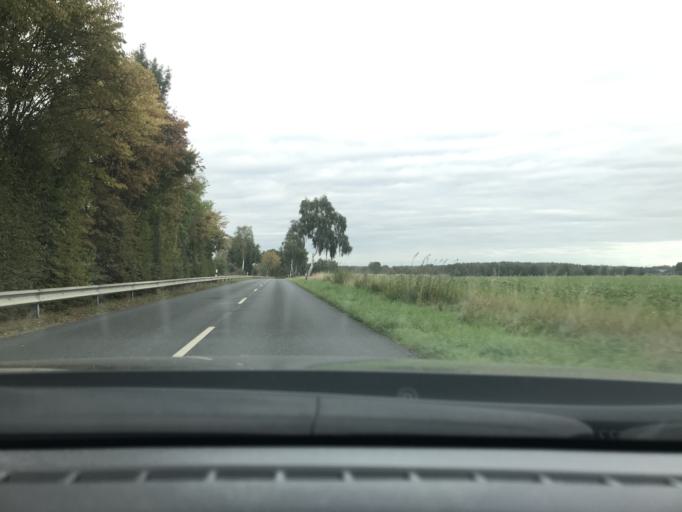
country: DE
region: Lower Saxony
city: Suderburg
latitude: 52.9081
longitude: 10.4371
